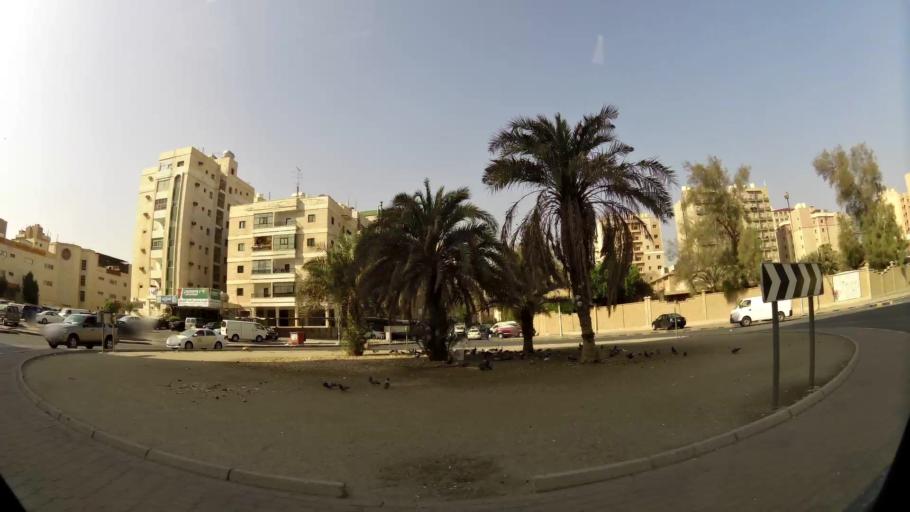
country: KW
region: Muhafazat Hawalli
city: Hawalli
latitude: 29.3342
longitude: 48.0229
